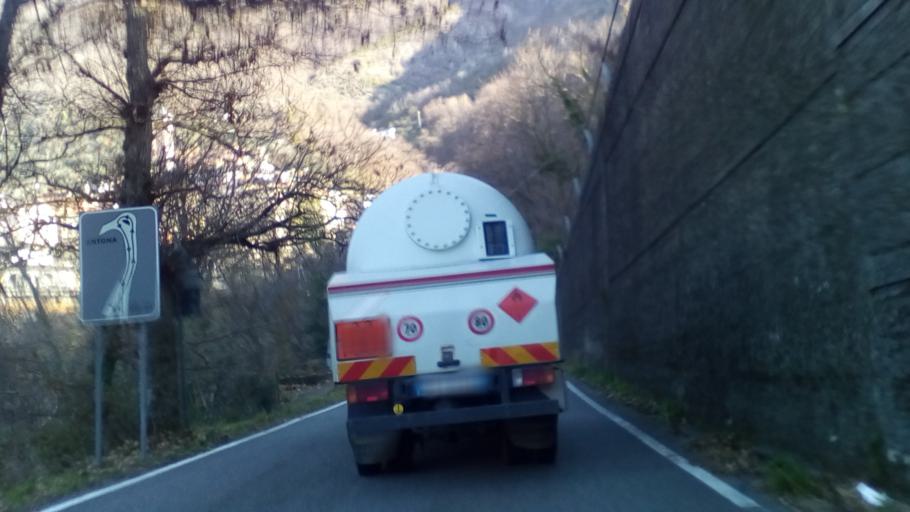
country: IT
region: Tuscany
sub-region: Provincia di Massa-Carrara
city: Montignoso
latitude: 44.0560
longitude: 10.1818
